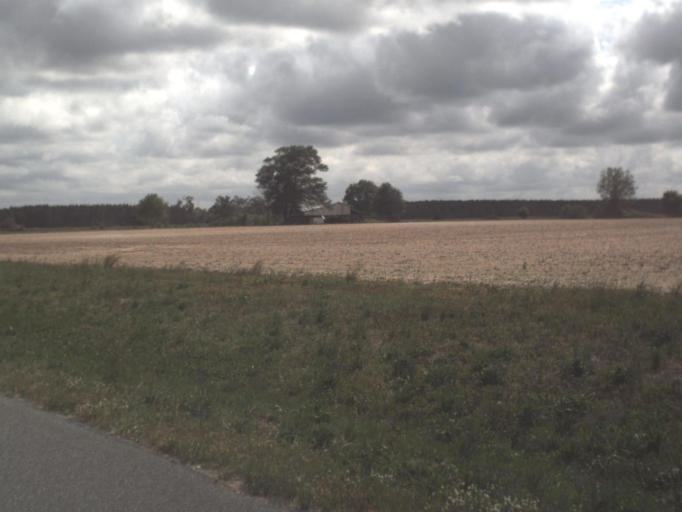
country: US
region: Florida
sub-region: Santa Rosa County
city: Point Baker
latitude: 30.7722
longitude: -87.0928
